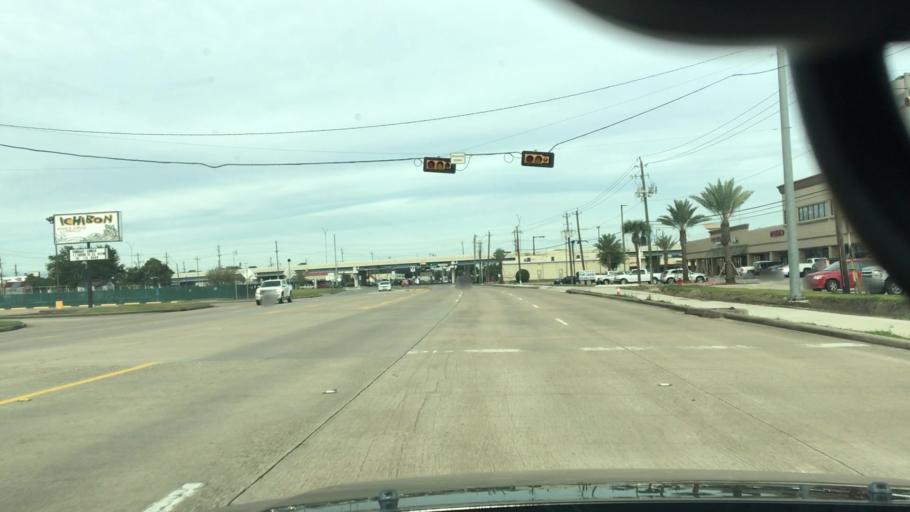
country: US
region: Texas
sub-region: Harris County
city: Nassau Bay
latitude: 29.5440
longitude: -95.1043
